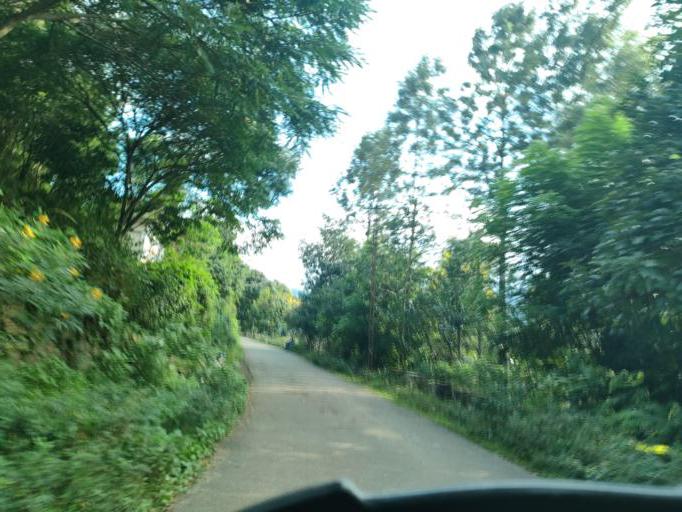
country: IN
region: Tamil Nadu
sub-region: Dindigul
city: Kodaikanal
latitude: 10.2803
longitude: 77.5293
